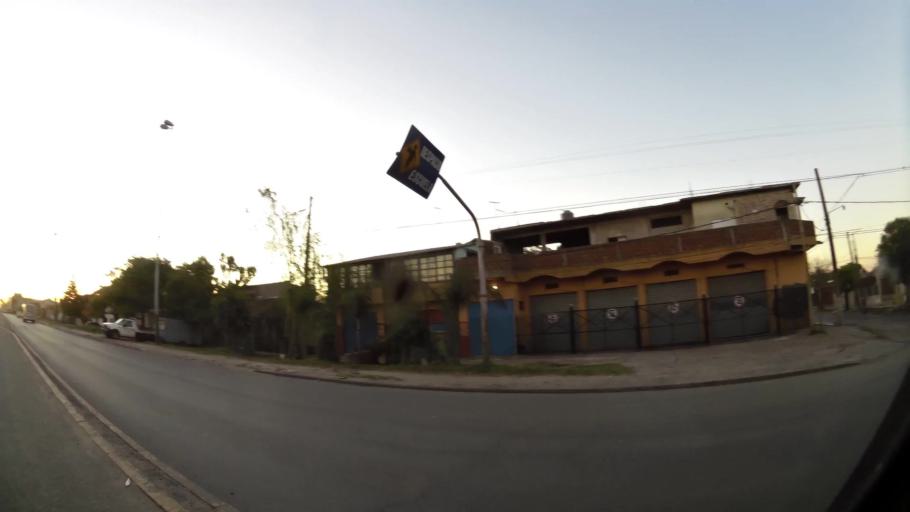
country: AR
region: Buenos Aires
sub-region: Partido de Almirante Brown
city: Adrogue
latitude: -34.7938
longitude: -58.3160
